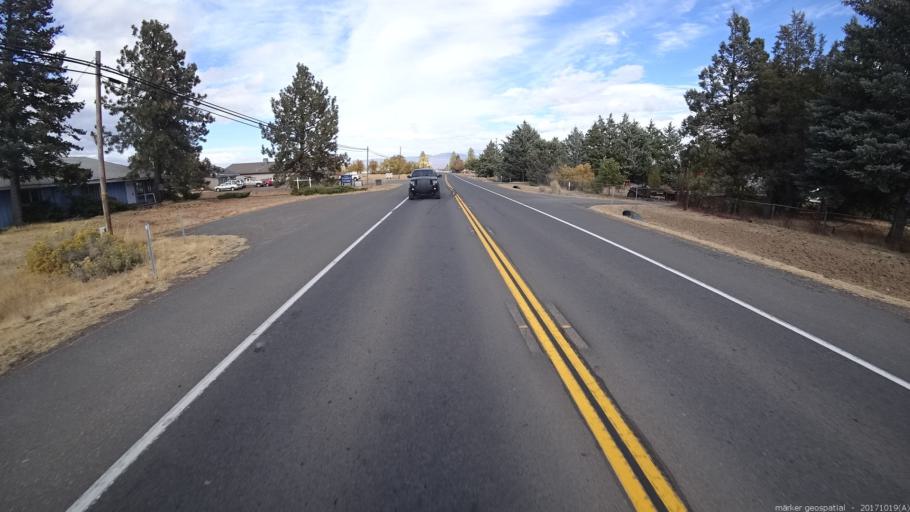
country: US
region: California
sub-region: Shasta County
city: Burney
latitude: 41.0214
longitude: -121.4270
